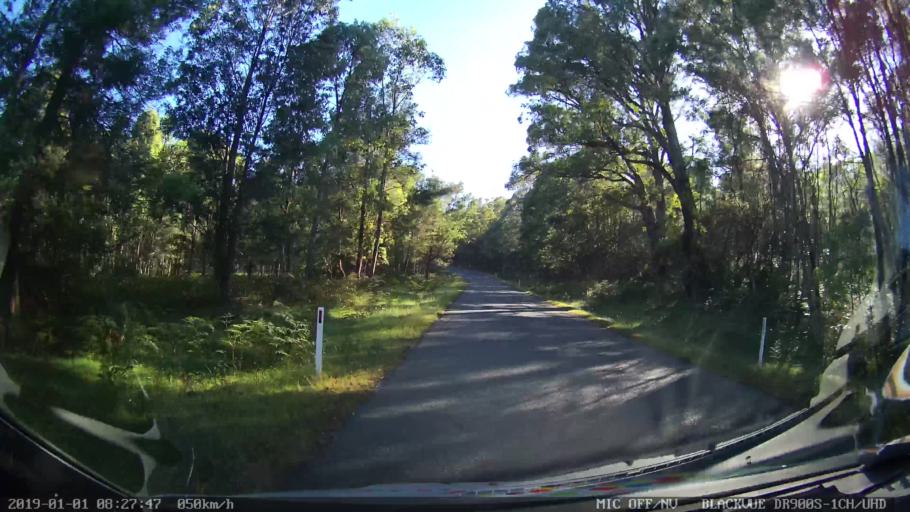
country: AU
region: New South Wales
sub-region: Snowy River
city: Jindabyne
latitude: -36.3795
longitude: 148.1858
